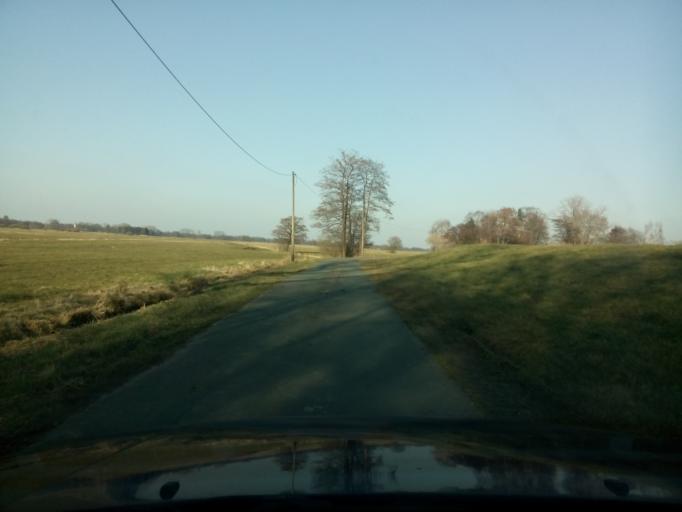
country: DE
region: Lower Saxony
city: Osterholz-Scharmbeck
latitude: 53.1619
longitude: 8.8015
